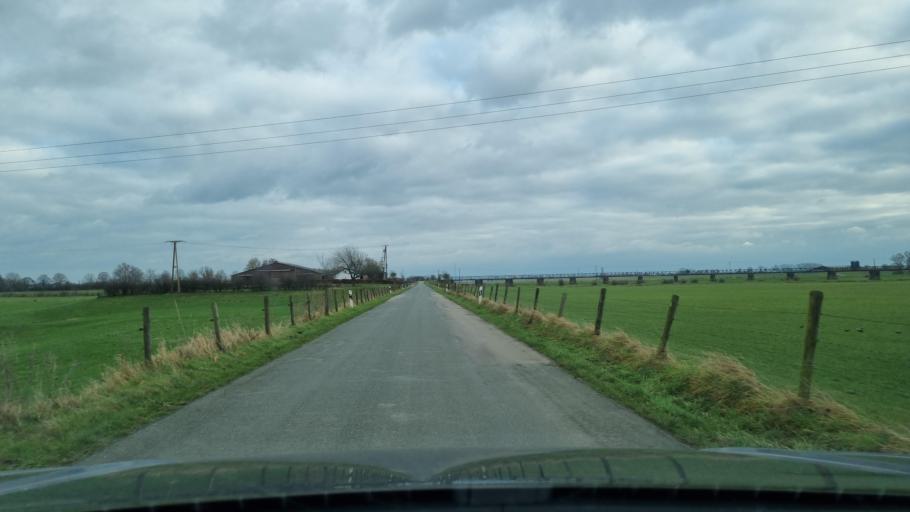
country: DE
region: North Rhine-Westphalia
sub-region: Regierungsbezirk Dusseldorf
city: Kleve
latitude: 51.8297
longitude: 6.1613
